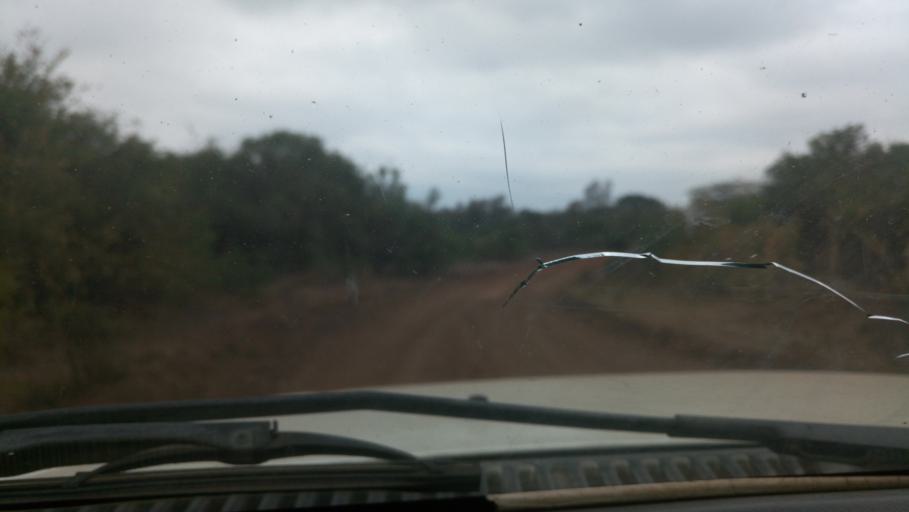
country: KE
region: Nairobi Area
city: Nairobi
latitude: -1.3724
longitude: 36.7693
